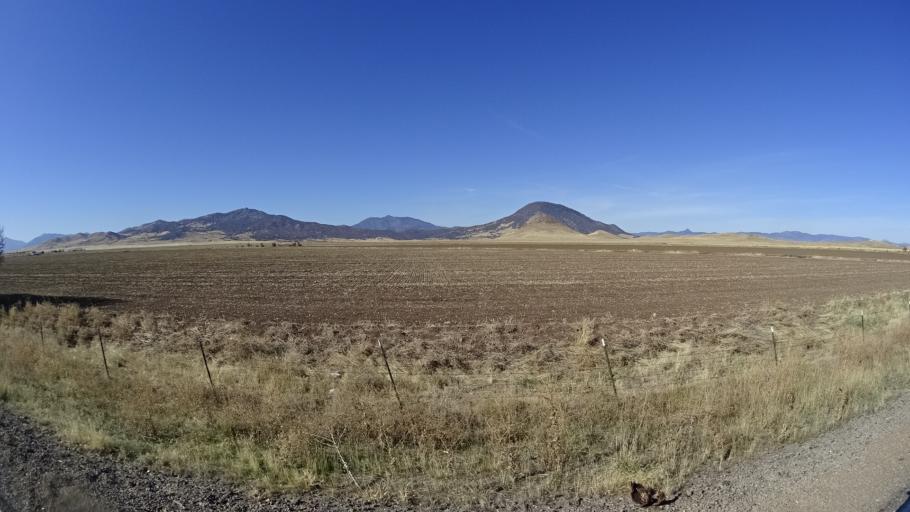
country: US
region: California
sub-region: Siskiyou County
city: Montague
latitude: 41.7989
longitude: -122.4503
